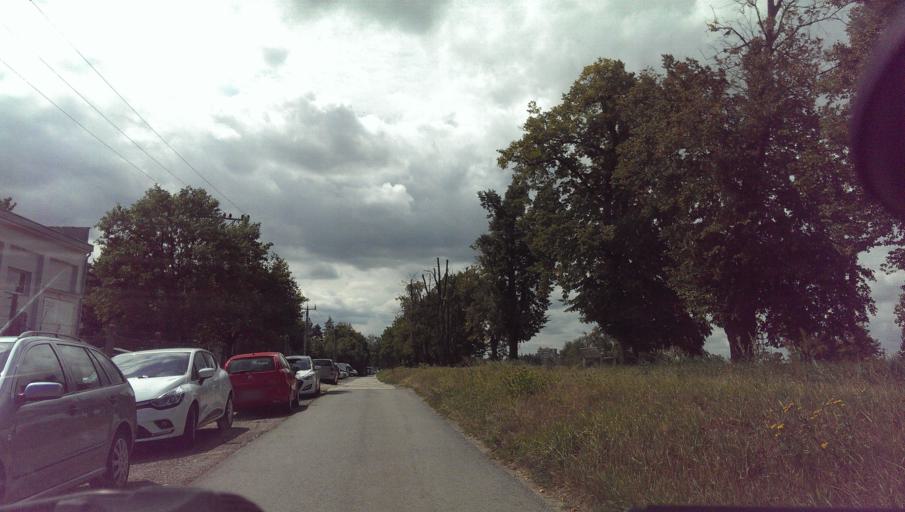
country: CZ
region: Zlin
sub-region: Okres Uherske Hradiste
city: Uherske Hradiste
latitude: 49.0767
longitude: 17.4764
